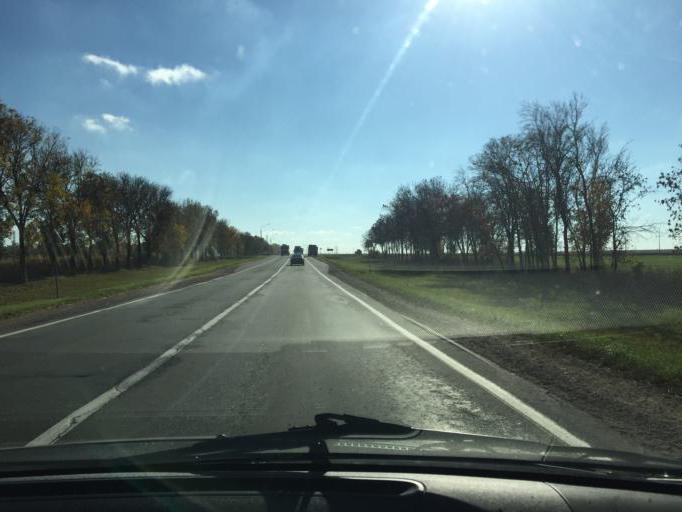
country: BY
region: Minsk
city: Salihorsk
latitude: 52.8757
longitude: 27.4674
